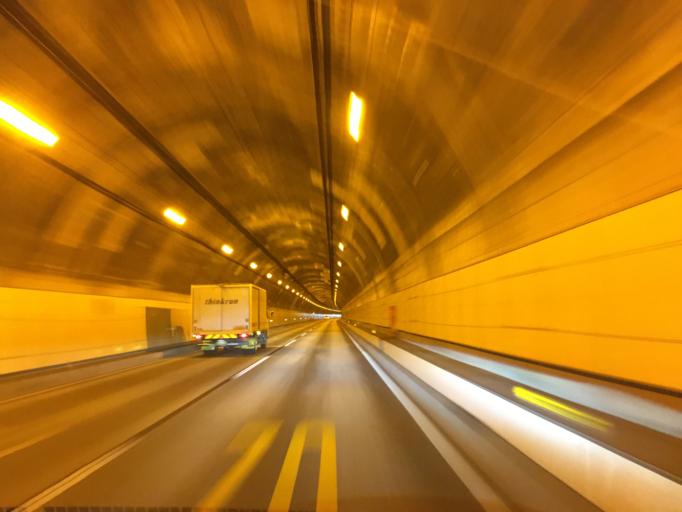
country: JP
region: Kanagawa
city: Ninomiya
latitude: 35.2952
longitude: 139.2110
